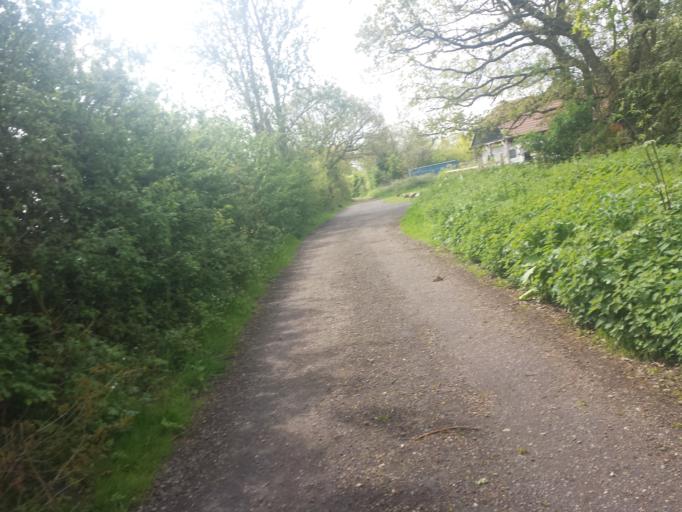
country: GB
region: England
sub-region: Essex
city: Great Bentley
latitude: 51.8814
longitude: 1.0443
